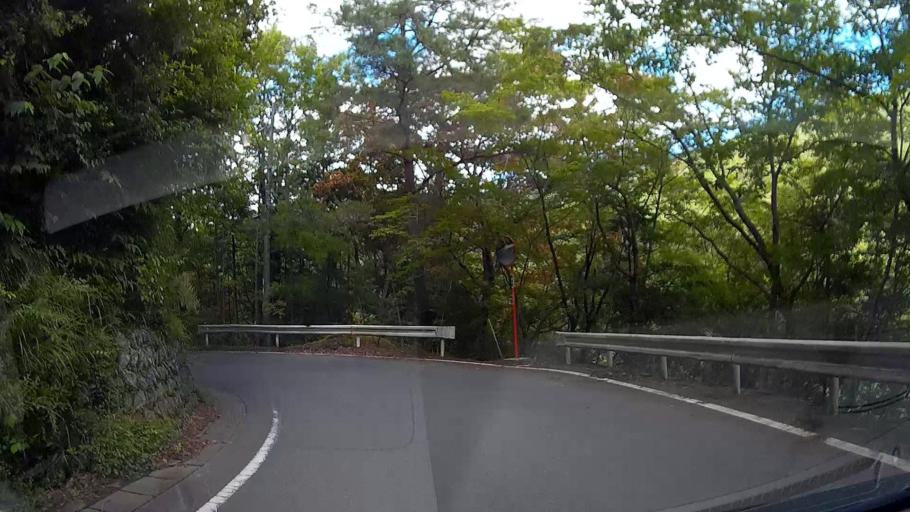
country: JP
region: Shizuoka
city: Shizuoka-shi
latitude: 35.2339
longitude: 138.2531
